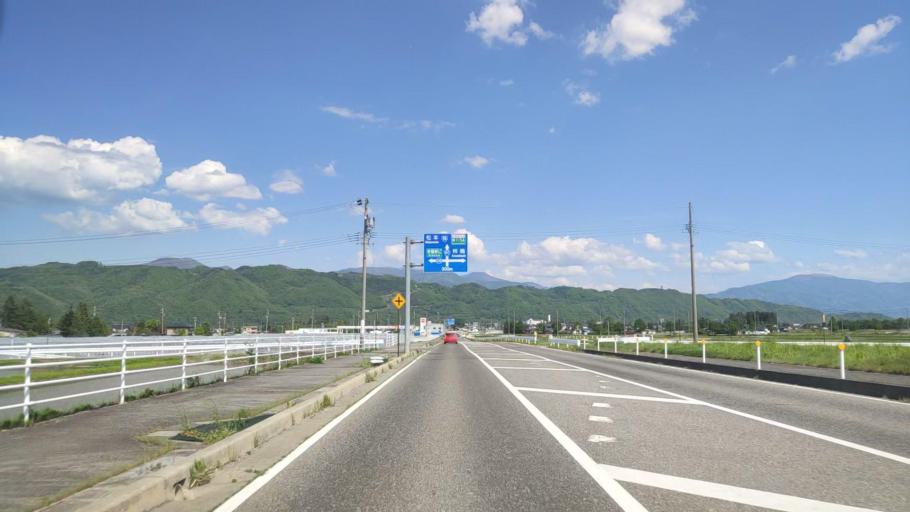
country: JP
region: Nagano
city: Toyoshina
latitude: 36.2807
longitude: 137.9171
